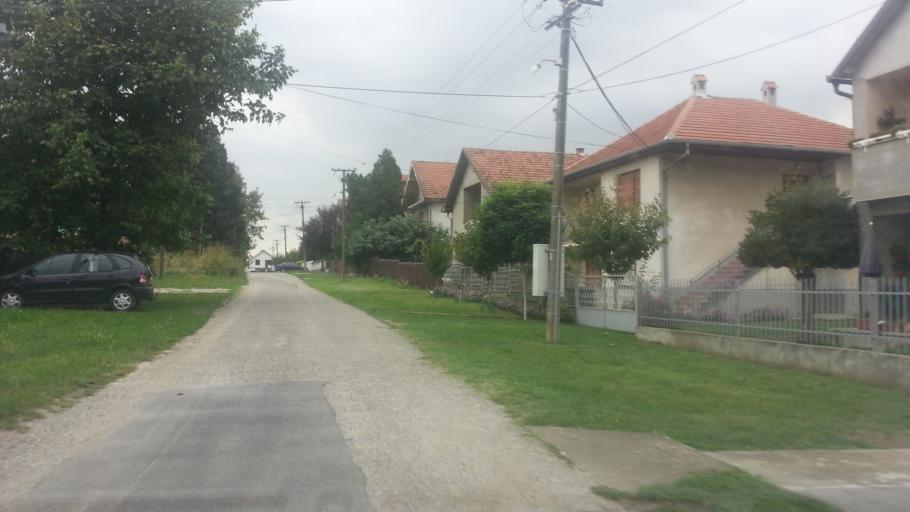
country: RS
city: Stari Banovci
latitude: 44.9758
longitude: 20.2774
